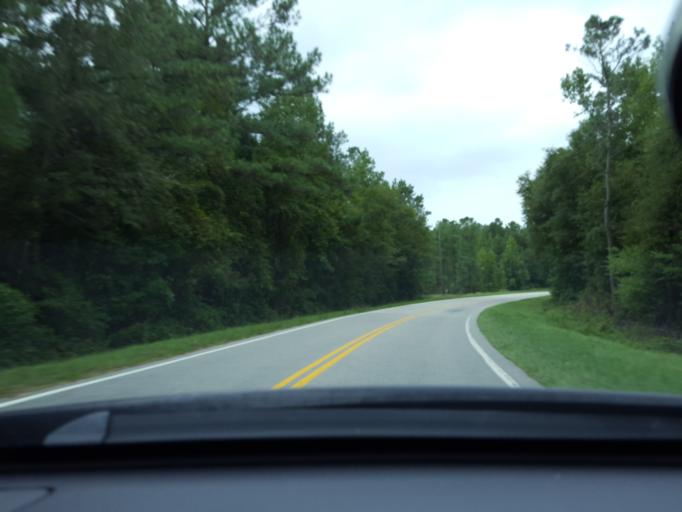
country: US
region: North Carolina
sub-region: Sampson County
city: Clinton
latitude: 34.7862
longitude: -78.3225
